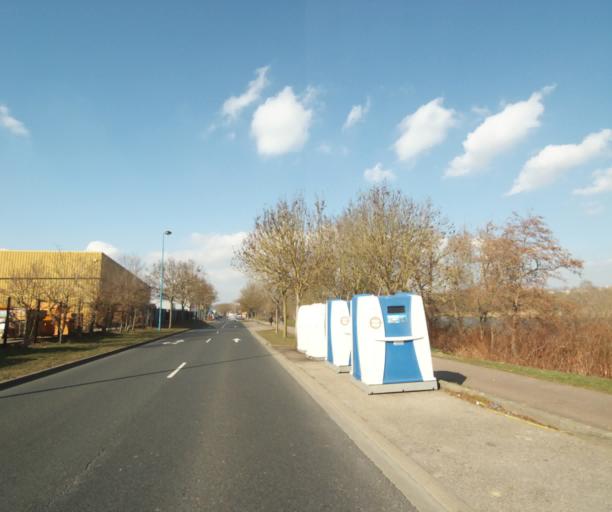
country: FR
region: Lorraine
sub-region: Departement de Meurthe-et-Moselle
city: Tomblaine
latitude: 48.6819
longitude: 6.2068
